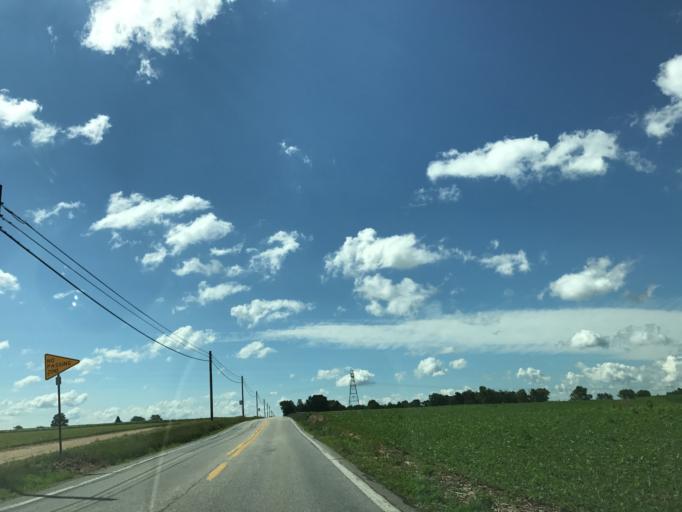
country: US
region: Pennsylvania
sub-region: Lancaster County
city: Rheems
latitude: 40.1205
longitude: -76.5973
